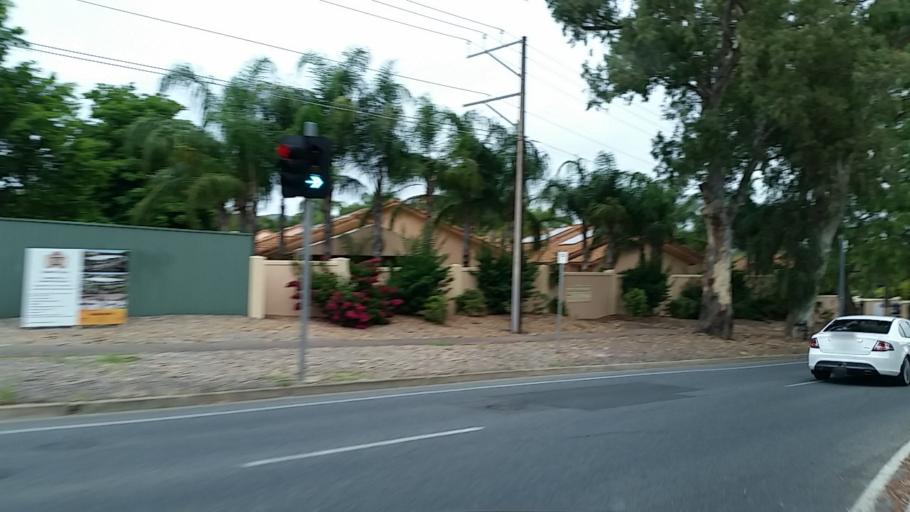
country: AU
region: South Australia
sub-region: Campbelltown
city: Paradise
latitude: -34.8640
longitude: 138.6801
